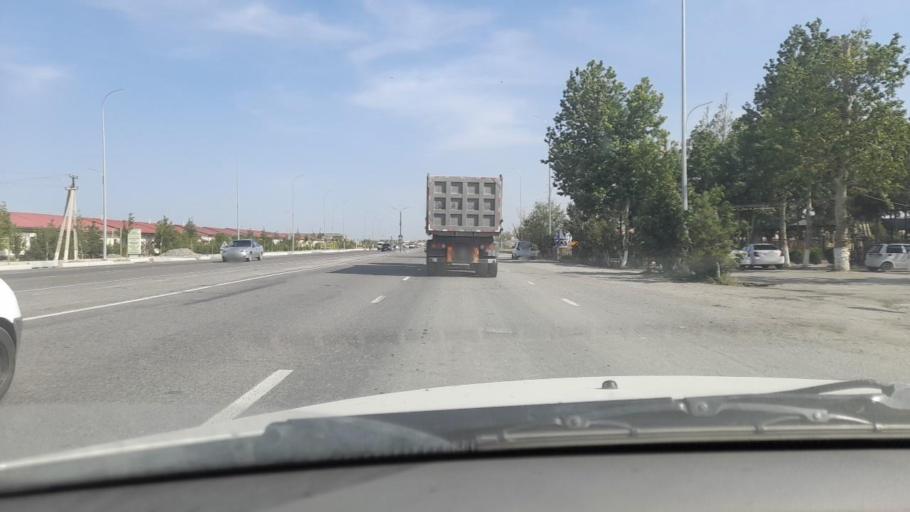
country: UZ
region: Samarqand
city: Daxbet
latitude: 39.7351
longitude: 66.9328
